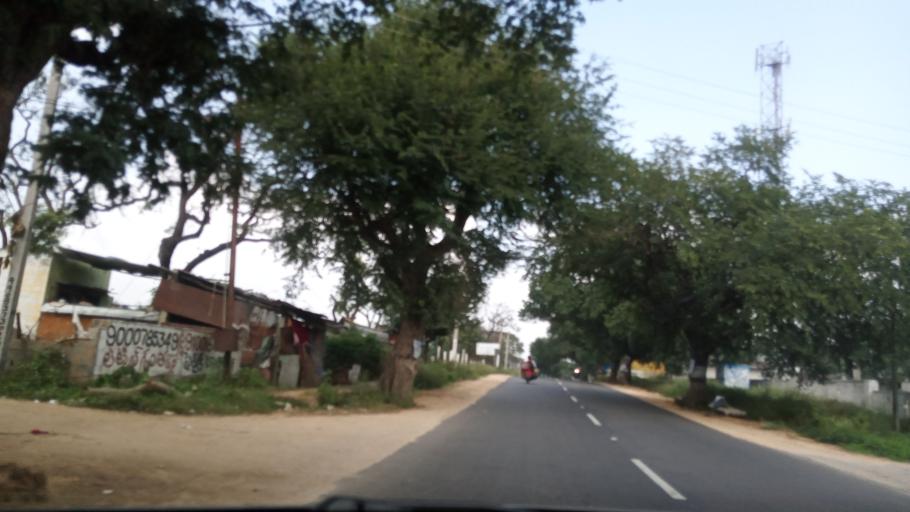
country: IN
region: Andhra Pradesh
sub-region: Chittoor
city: Madanapalle
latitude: 13.5957
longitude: 78.5281
